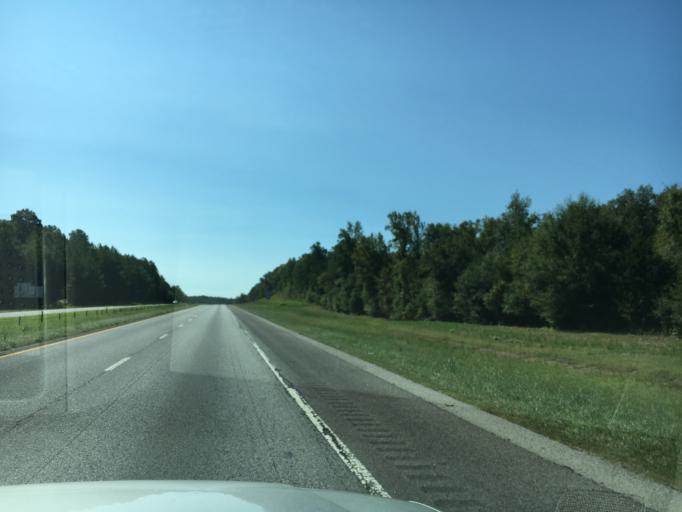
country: US
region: South Carolina
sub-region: Spartanburg County
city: Roebuck
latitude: 34.8327
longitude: -81.9686
